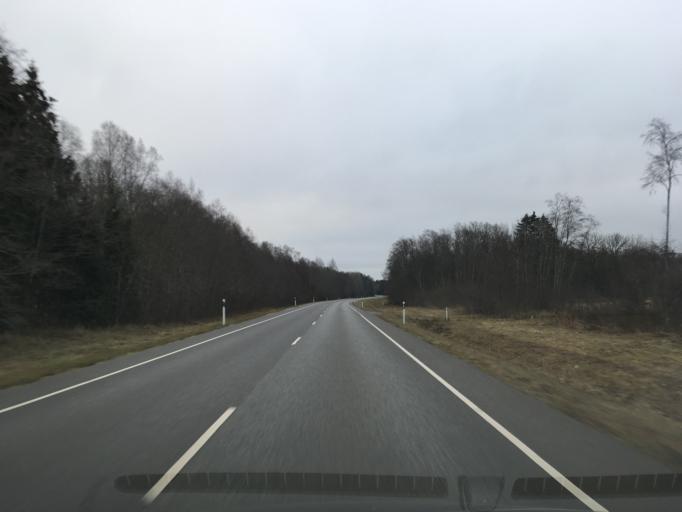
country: EE
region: Laeaene-Virumaa
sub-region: Kadrina vald
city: Kadrina
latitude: 59.4499
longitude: 26.0516
